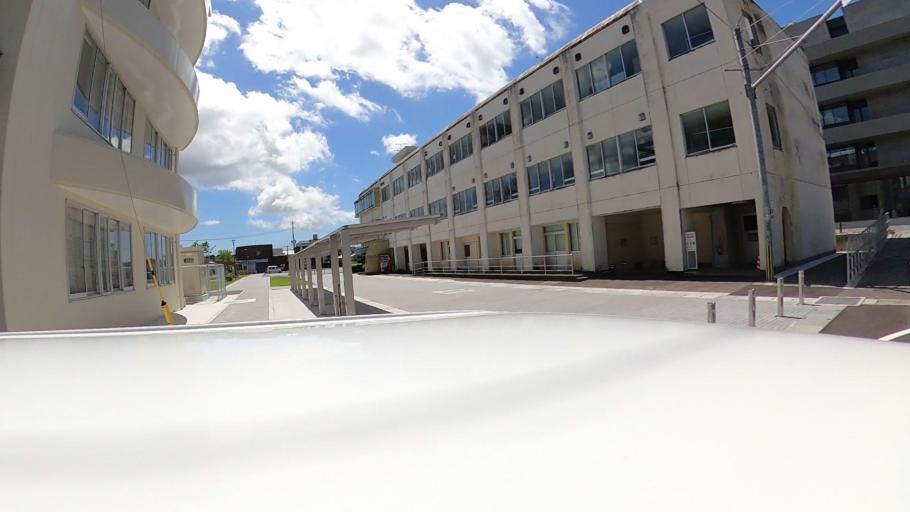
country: JP
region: Miyazaki
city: Tsuma
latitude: 32.1084
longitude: 131.4009
